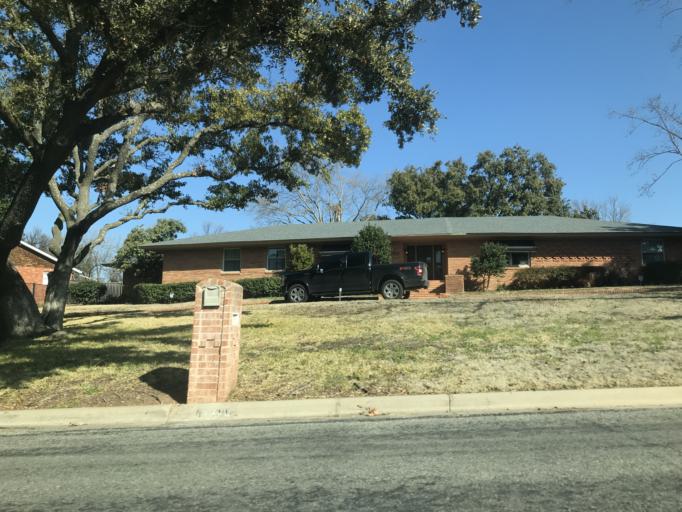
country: US
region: Texas
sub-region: Tom Green County
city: San Angelo
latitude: 31.4353
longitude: -100.4693
